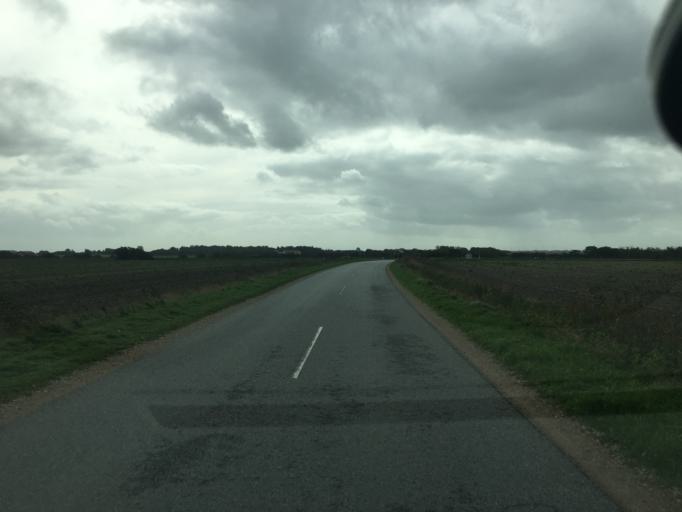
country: DE
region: Schleswig-Holstein
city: Aventoft
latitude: 54.9617
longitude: 8.7648
